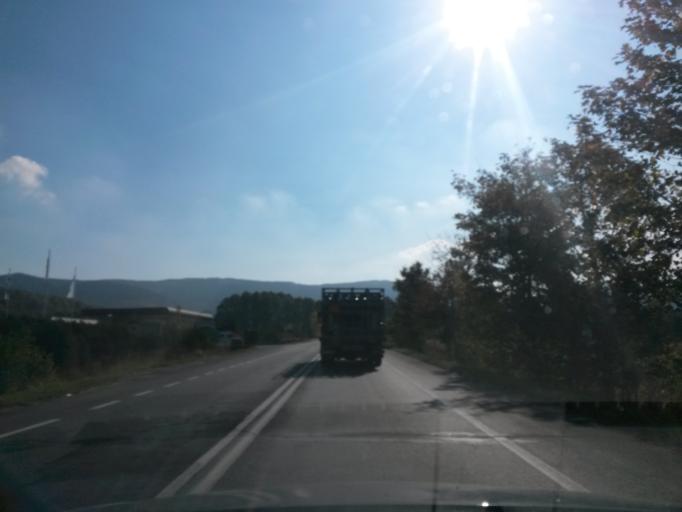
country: PL
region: Lower Silesian Voivodeship
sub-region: Powiat jeleniogorski
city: Kowary
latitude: 50.8005
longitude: 15.8401
